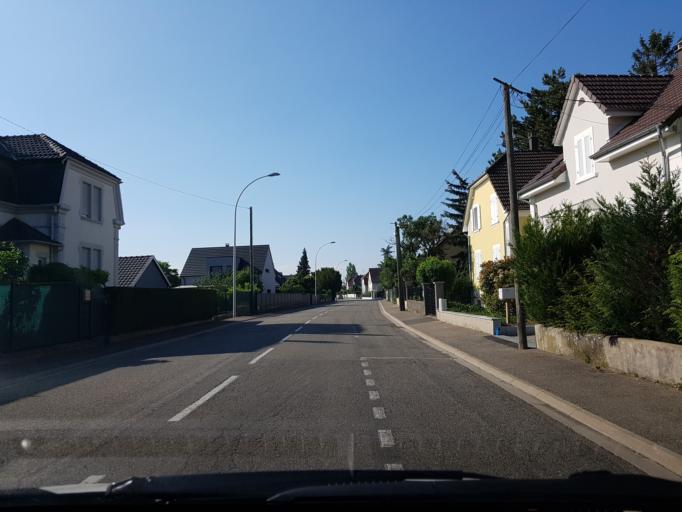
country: FR
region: Alsace
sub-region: Departement du Haut-Rhin
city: Rixheim
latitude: 47.7482
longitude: 7.3983
